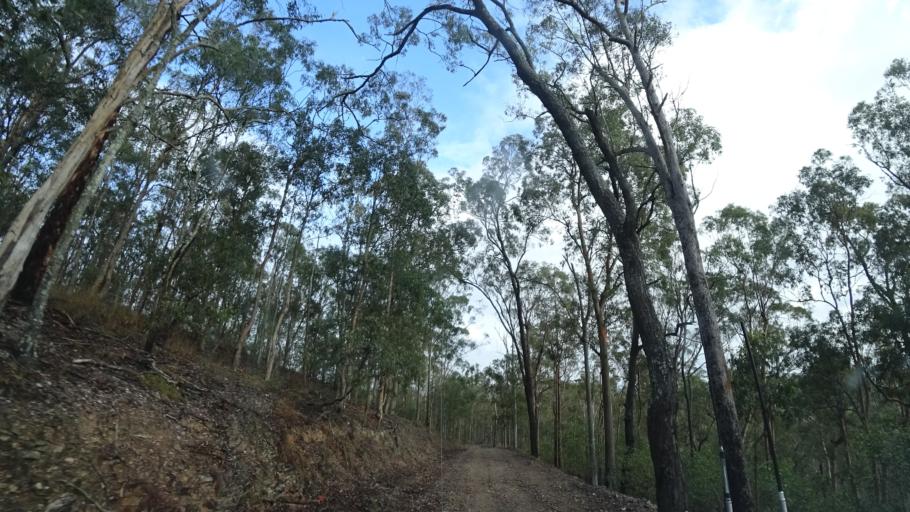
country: AU
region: Queensland
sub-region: Brisbane
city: Kenmore Hills
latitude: -27.4599
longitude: 152.9207
